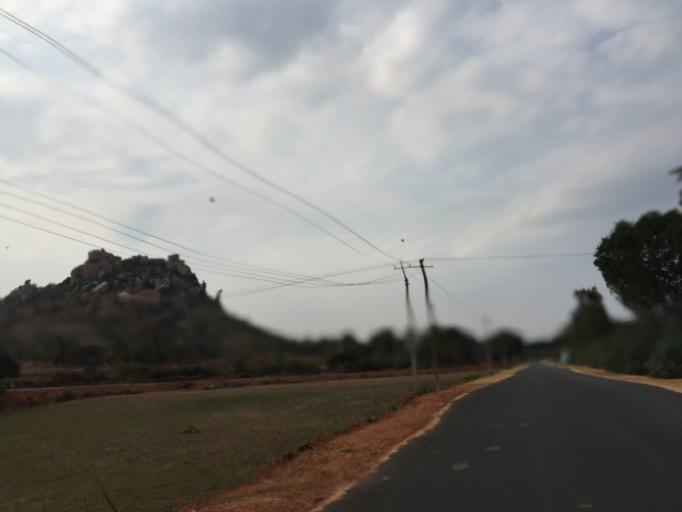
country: IN
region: Karnataka
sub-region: Chikkaballapur
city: Gudibanda
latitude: 13.5604
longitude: 77.7375
